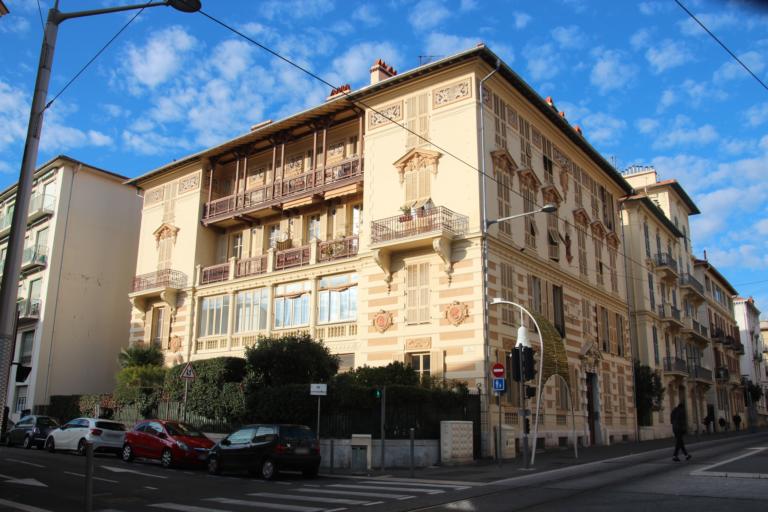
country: FR
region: Provence-Alpes-Cote d'Azur
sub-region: Departement des Alpes-Maritimes
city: Nice
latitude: 43.7114
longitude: 7.2619
